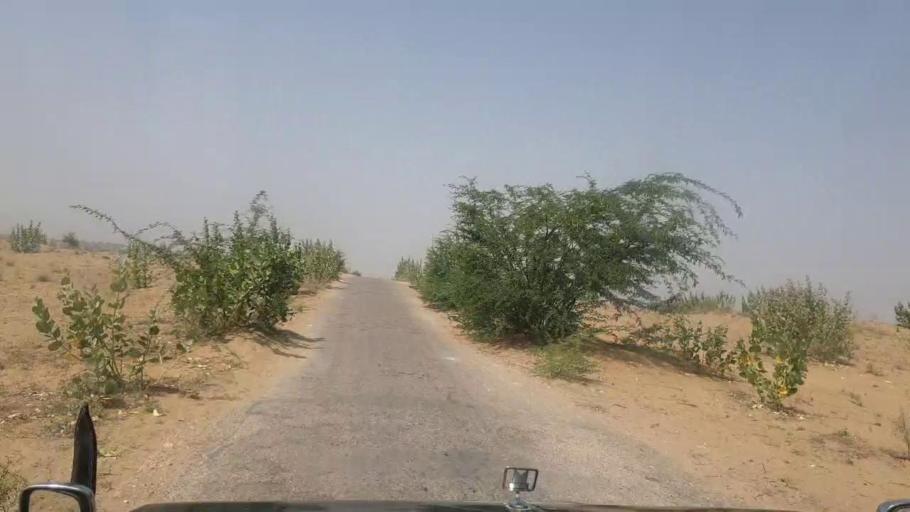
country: PK
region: Sindh
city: Islamkot
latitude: 25.1190
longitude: 70.2349
